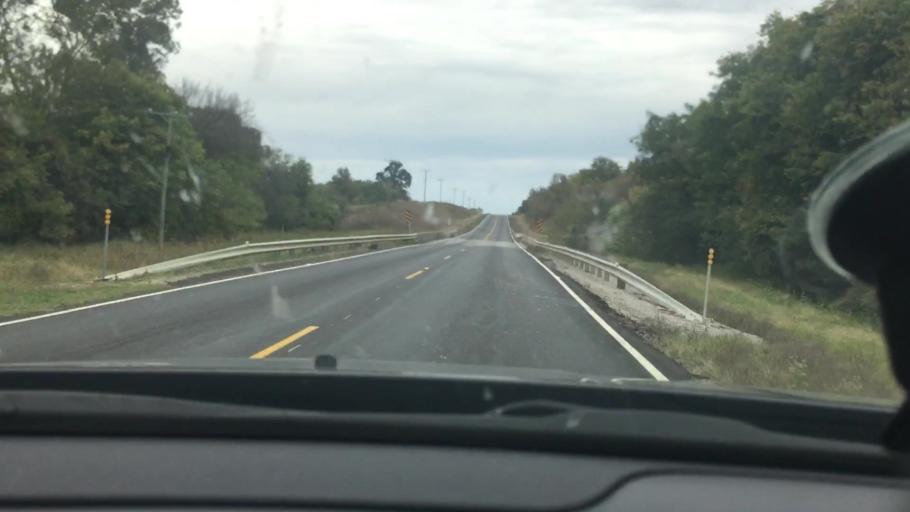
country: US
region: Oklahoma
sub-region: Coal County
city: Coalgate
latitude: 34.4061
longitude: -96.4245
